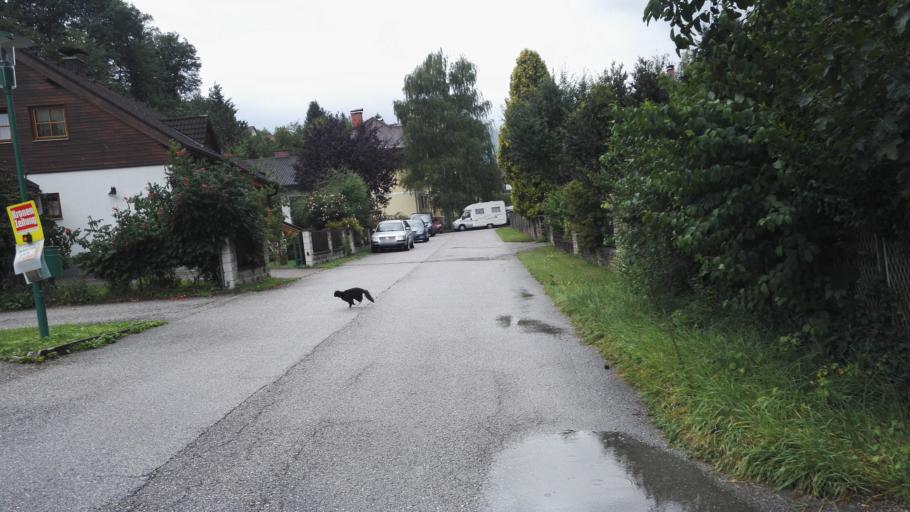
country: AT
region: Lower Austria
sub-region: Politischer Bezirk Neunkirchen
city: Payerbach
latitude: 47.6901
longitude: 15.8674
